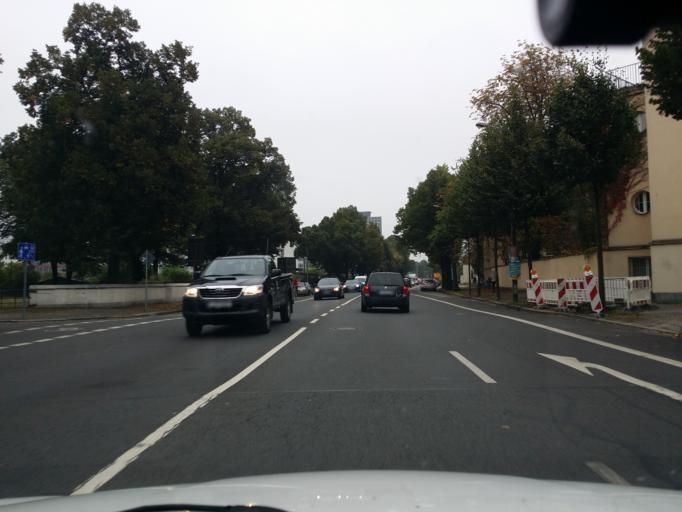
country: DE
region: Saxony
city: Leipzig
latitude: 51.3237
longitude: 12.3966
